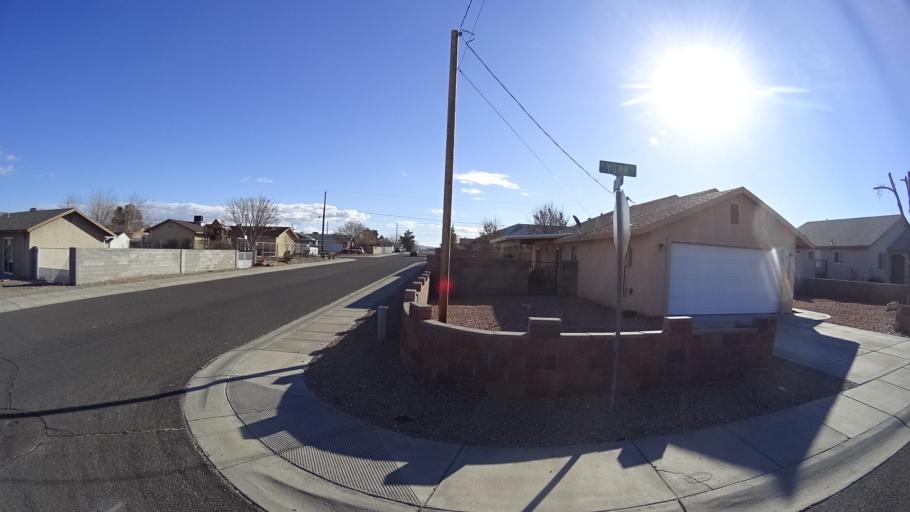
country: US
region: Arizona
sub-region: Mohave County
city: New Kingman-Butler
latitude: 35.2192
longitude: -113.9968
